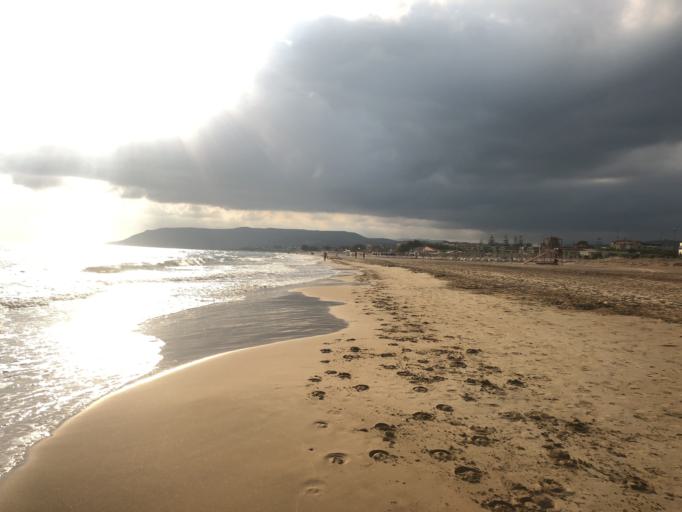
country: GR
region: Crete
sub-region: Nomos Chanias
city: Georgioupolis
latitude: 35.3547
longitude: 24.2917
